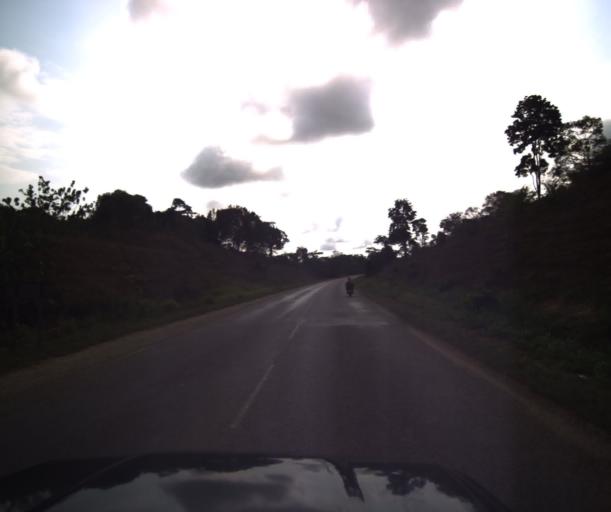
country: CM
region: Littoral
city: Dizangue
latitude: 3.9507
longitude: 10.0133
